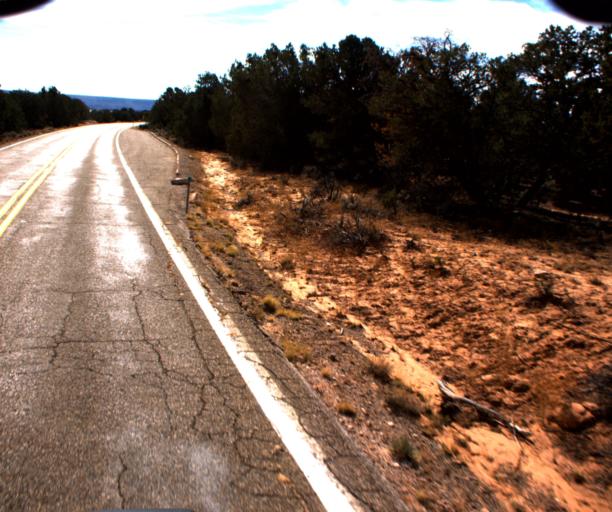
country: US
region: Arizona
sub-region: Navajo County
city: Kayenta
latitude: 36.6383
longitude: -110.5107
